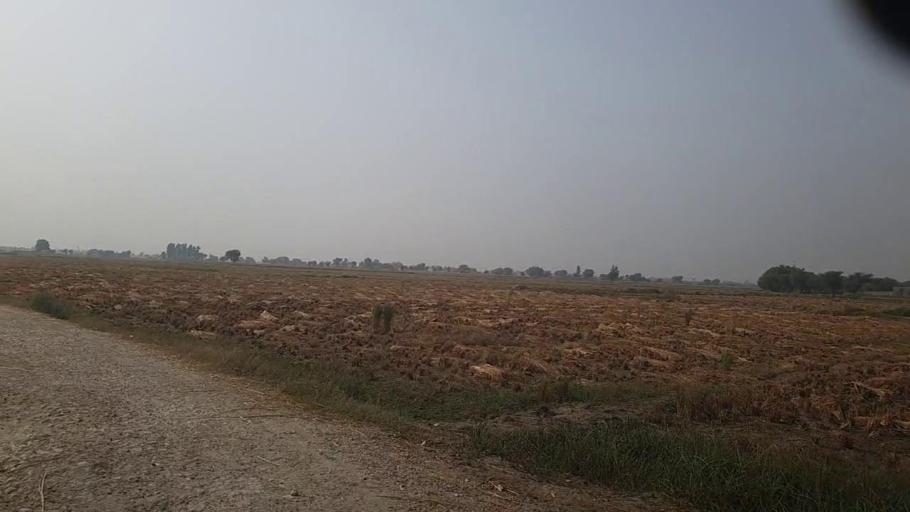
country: PK
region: Sindh
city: Kashmor
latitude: 28.3832
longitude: 69.4301
